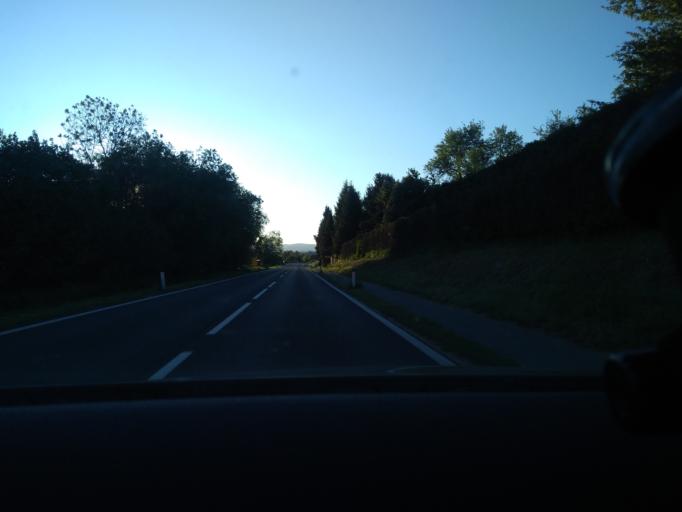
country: AT
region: Styria
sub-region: Politischer Bezirk Graz-Umgebung
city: Lieboch
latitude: 46.9858
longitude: 15.3105
